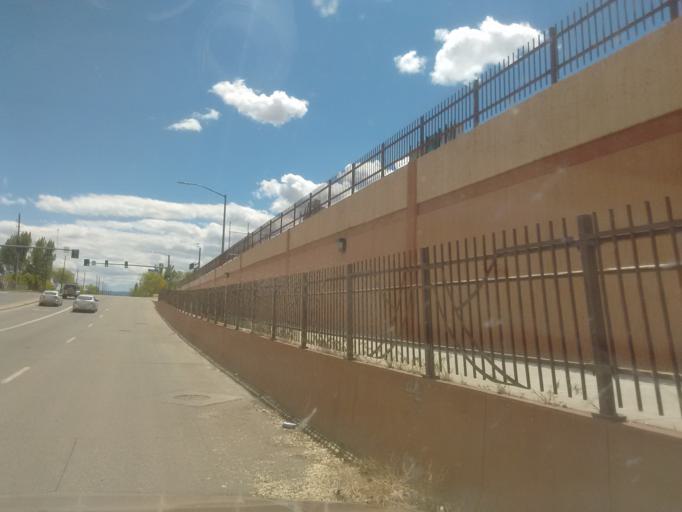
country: US
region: Colorado
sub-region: Mesa County
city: Fruitvale
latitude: 39.0766
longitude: -108.4966
